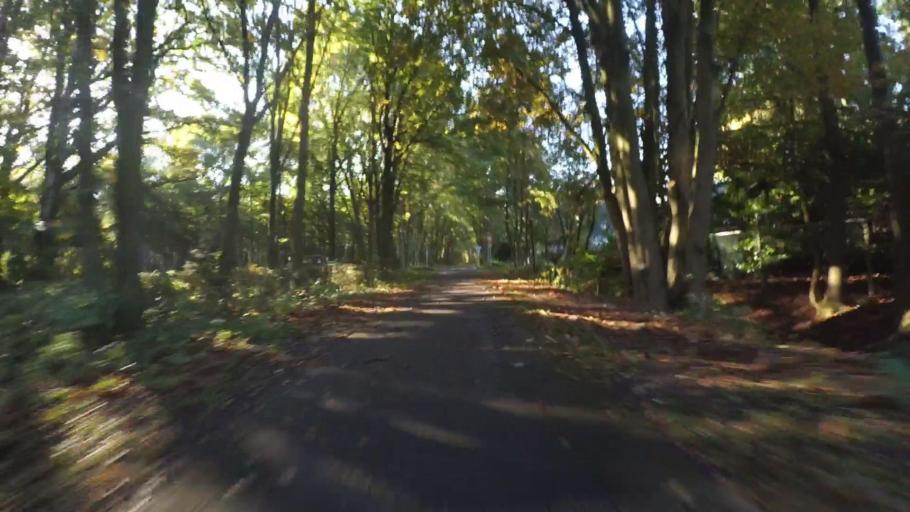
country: NL
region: Gelderland
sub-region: Gemeente Epe
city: Emst
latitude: 52.3034
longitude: 5.9851
